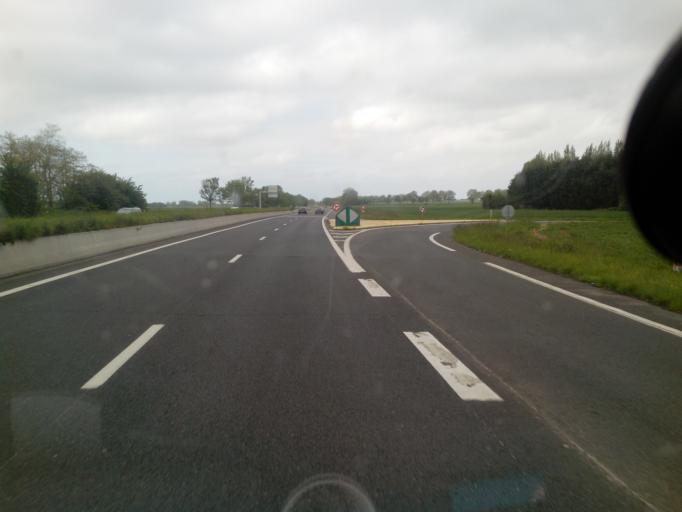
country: FR
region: Lower Normandy
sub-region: Departement du Calvados
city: Mathieu
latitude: 49.2590
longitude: -0.3830
